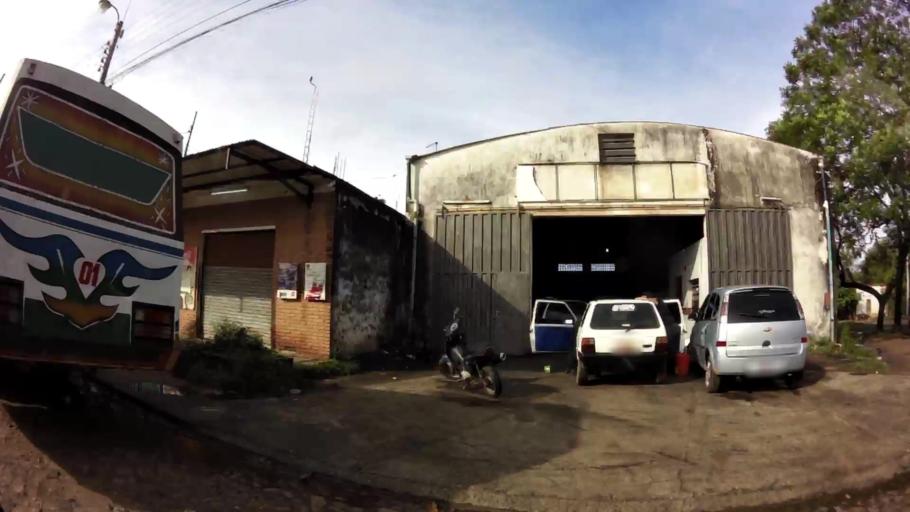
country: PY
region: Central
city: Limpio
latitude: -25.1720
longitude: -57.4839
